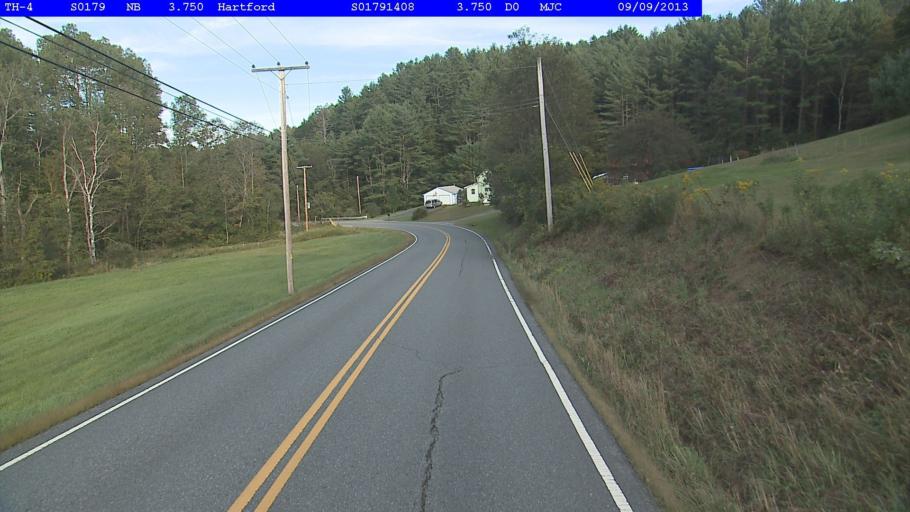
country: US
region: Vermont
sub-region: Windsor County
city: Woodstock
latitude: 43.6930
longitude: -72.4390
